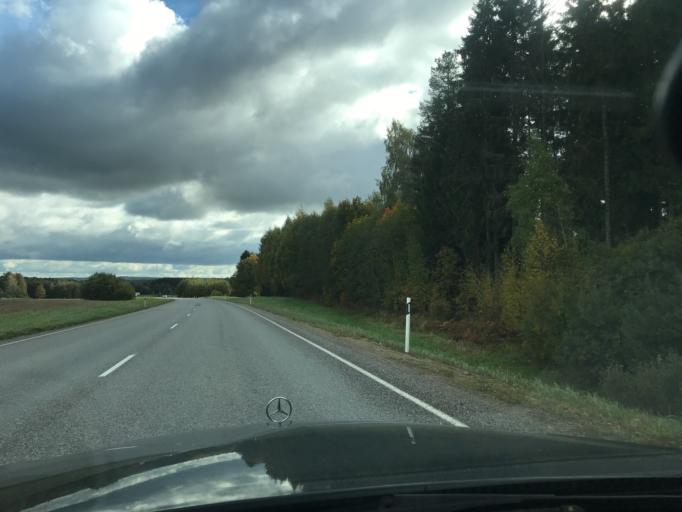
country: EE
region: Vorumaa
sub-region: Voru linn
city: Voru
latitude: 57.7429
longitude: 27.2548
